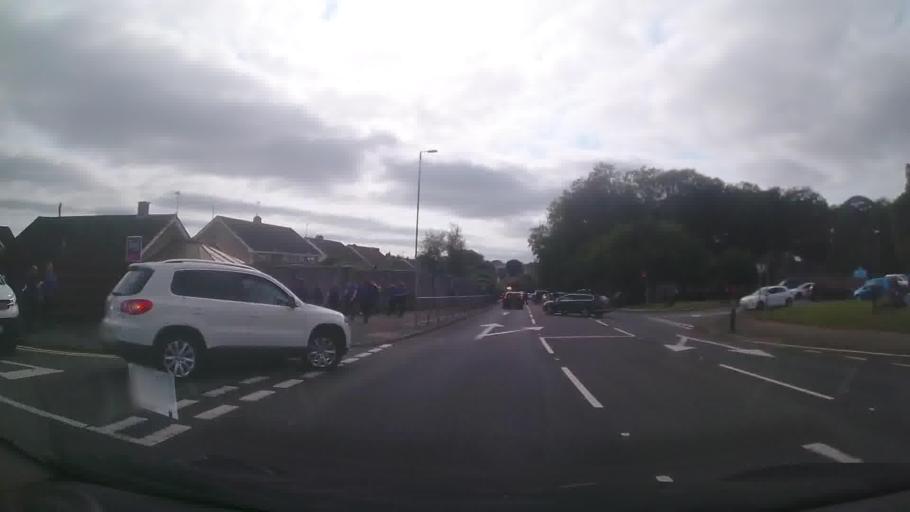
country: GB
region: Wales
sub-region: Pembrokeshire
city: Steynton
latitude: 51.7234
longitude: -5.0214
